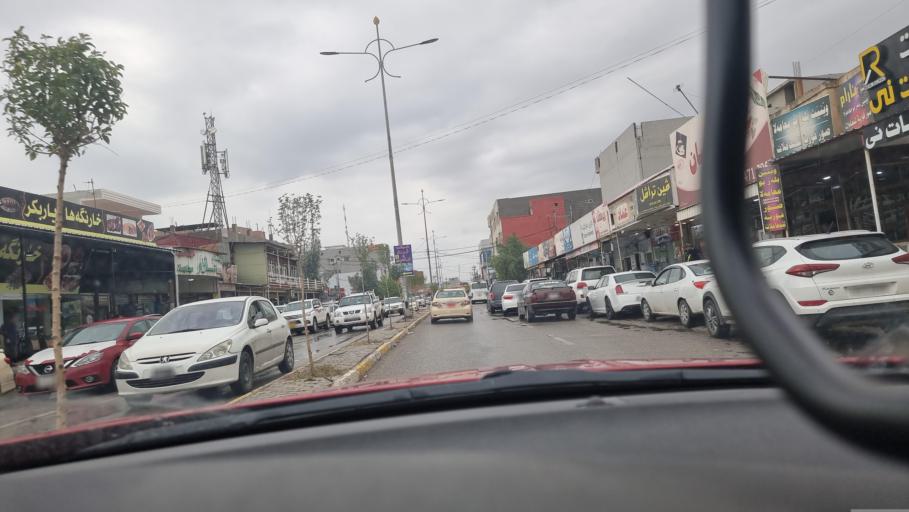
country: IQ
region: Dahuk
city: Saymayl
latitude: 36.8583
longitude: 42.8484
